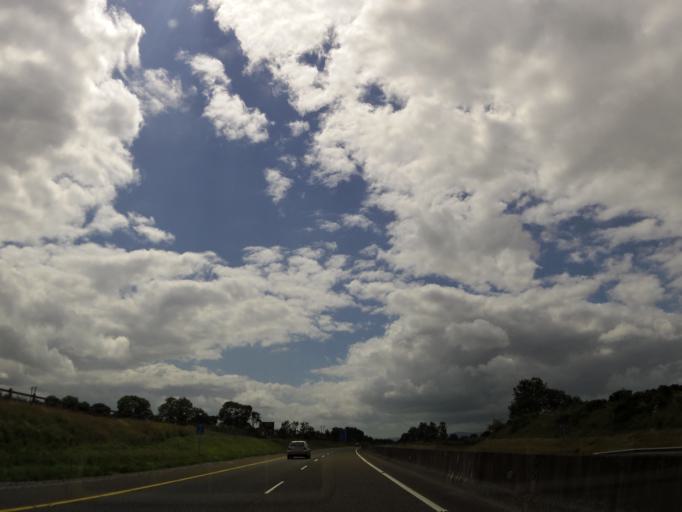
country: IE
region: Munster
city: Cashel
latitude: 52.5204
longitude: -7.8598
